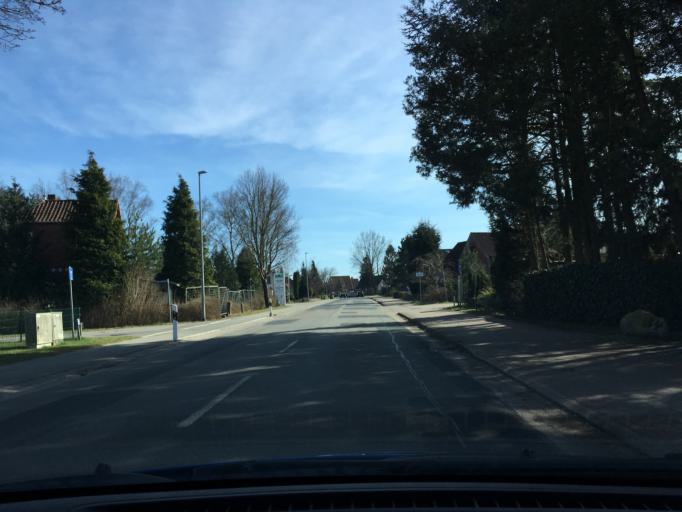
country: DE
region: Lower Saxony
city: Tespe
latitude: 53.3954
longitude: 10.4111
